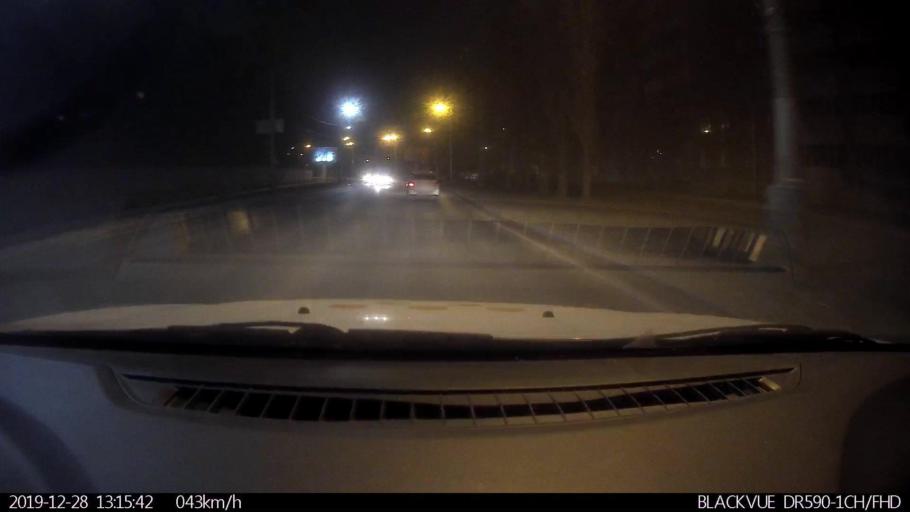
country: RU
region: Nizjnij Novgorod
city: Nizhniy Novgorod
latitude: 56.3271
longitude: 43.8678
